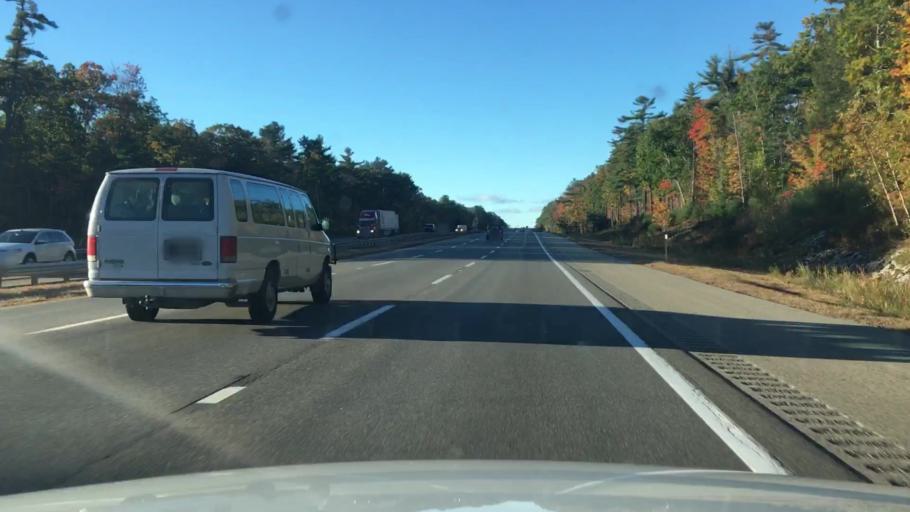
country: US
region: Maine
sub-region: York County
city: West Kennebunk
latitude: 43.3762
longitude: -70.5788
